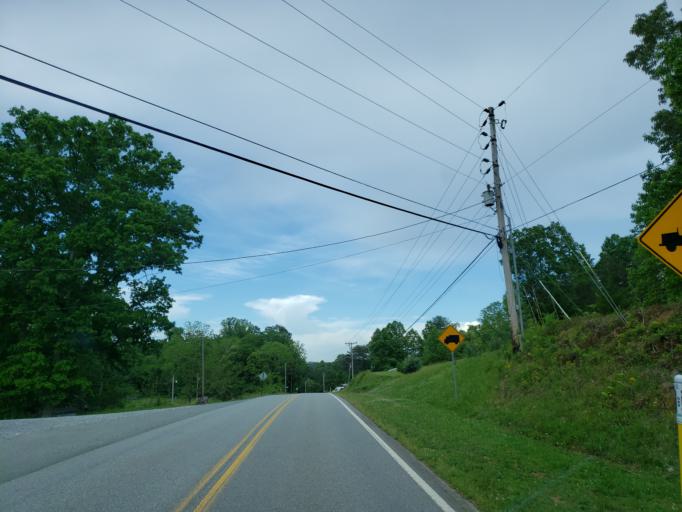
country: US
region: Georgia
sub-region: Fannin County
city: Blue Ridge
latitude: 34.8509
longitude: -84.3861
